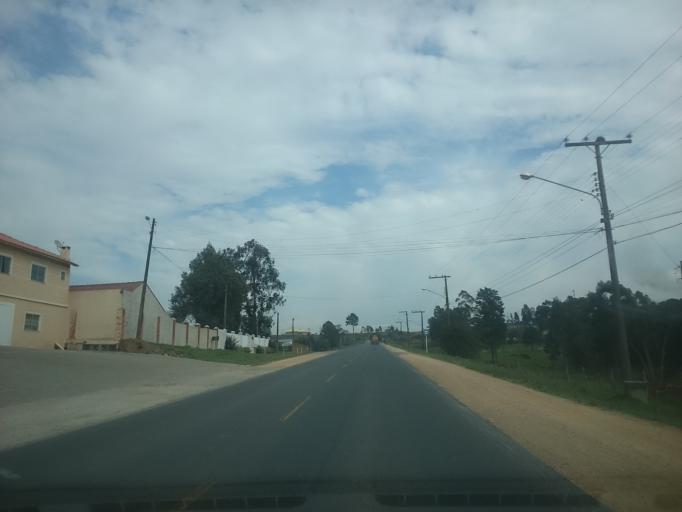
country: BR
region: Santa Catarina
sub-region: Lages
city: Lages
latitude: -27.7811
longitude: -50.3153
